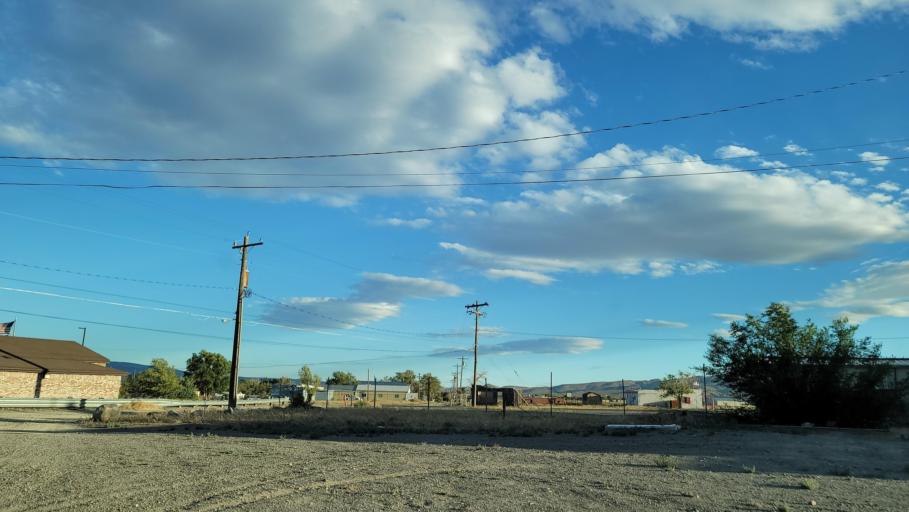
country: US
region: Nevada
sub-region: Lyon County
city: Silver Springs
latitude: 39.4154
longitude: -119.2242
